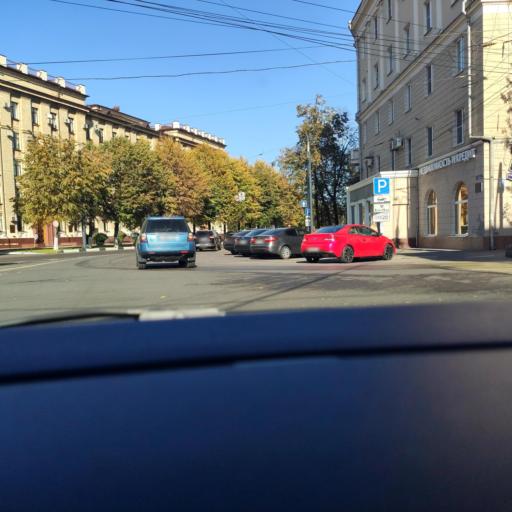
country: RU
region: Voronezj
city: Voronezh
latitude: 51.6590
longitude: 39.1987
